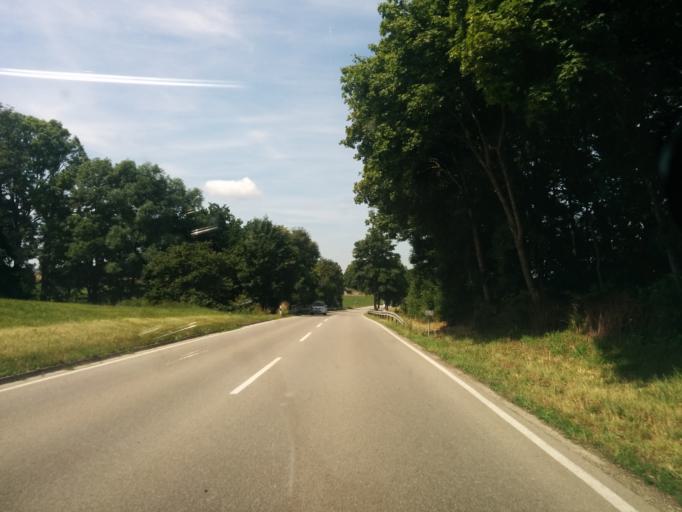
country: DE
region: Bavaria
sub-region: Upper Bavaria
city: Weil
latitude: 48.1391
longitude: 10.9586
